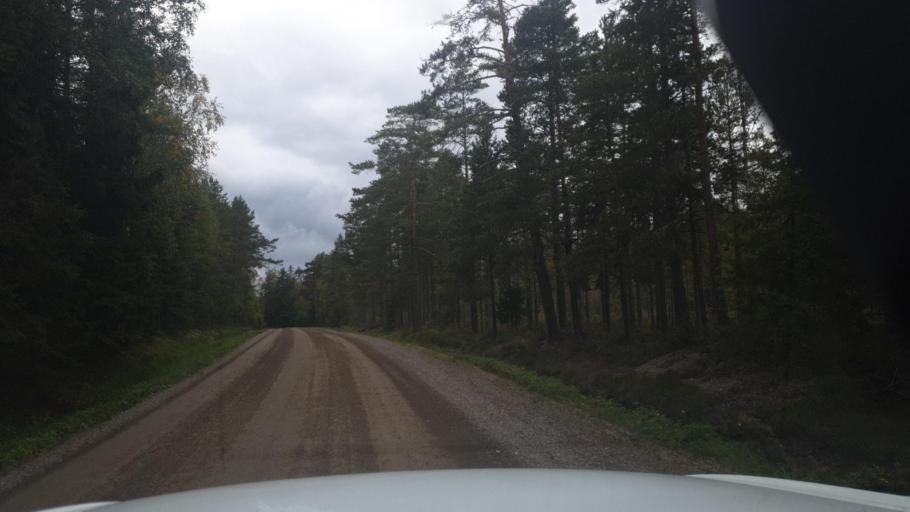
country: SE
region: Vaermland
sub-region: Sunne Kommun
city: Sunne
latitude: 59.8271
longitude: 12.8604
